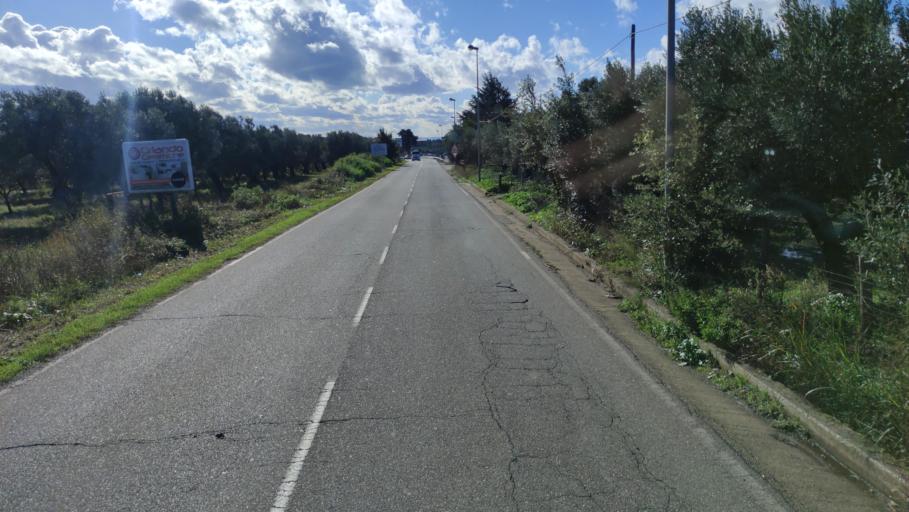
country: IT
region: Calabria
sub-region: Provincia di Catanzaro
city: Santa Eufemia Lamezia
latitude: 38.9268
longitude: 16.2845
